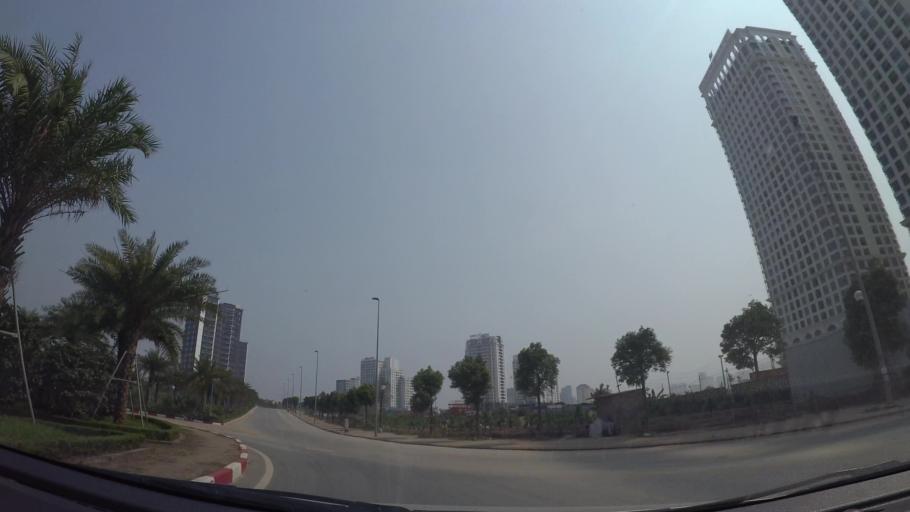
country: VN
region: Ha Noi
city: Tay Ho
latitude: 21.0842
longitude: 105.8134
